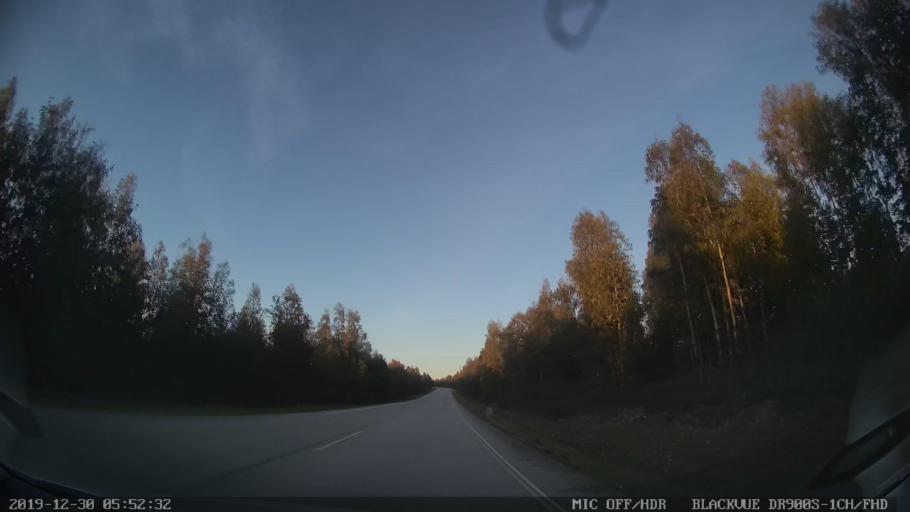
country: PT
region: Castelo Branco
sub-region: Idanha-A-Nova
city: Idanha-a-Nova
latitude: 40.0059
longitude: -7.2492
